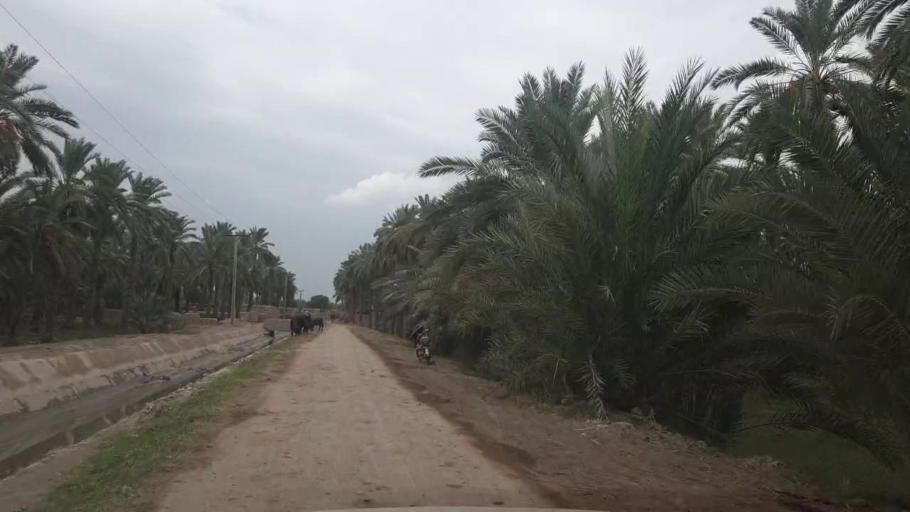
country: PK
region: Sindh
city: Khairpur
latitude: 27.6072
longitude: 68.8035
